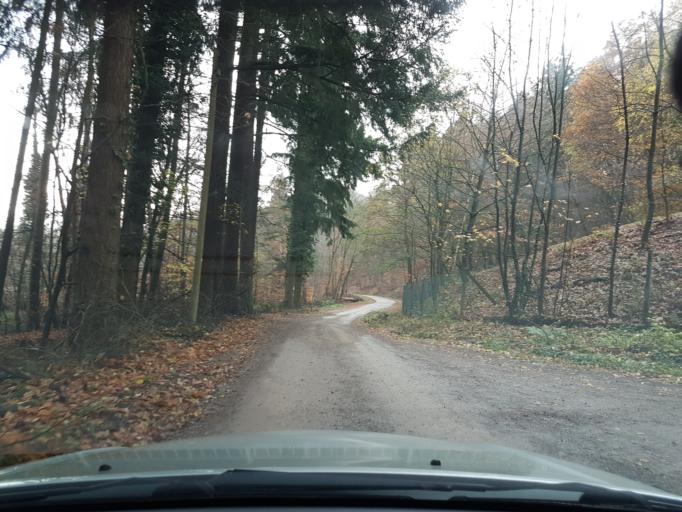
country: DE
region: Hesse
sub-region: Regierungsbezirk Darmstadt
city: Kiedrich
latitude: 50.0489
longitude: 8.0423
